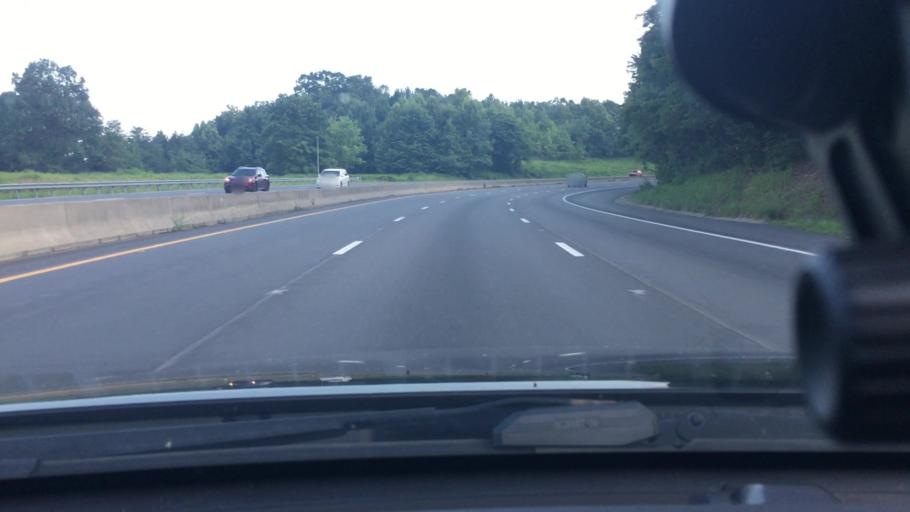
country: US
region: North Carolina
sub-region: Buncombe County
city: Black Mountain
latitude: 35.6210
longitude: -82.2397
